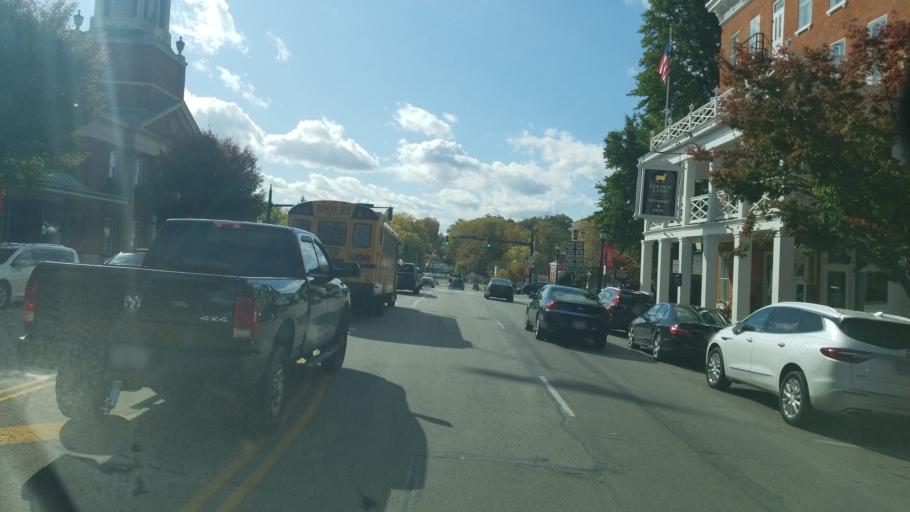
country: US
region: Ohio
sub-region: Warren County
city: Lebanon
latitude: 39.4342
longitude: -84.2083
